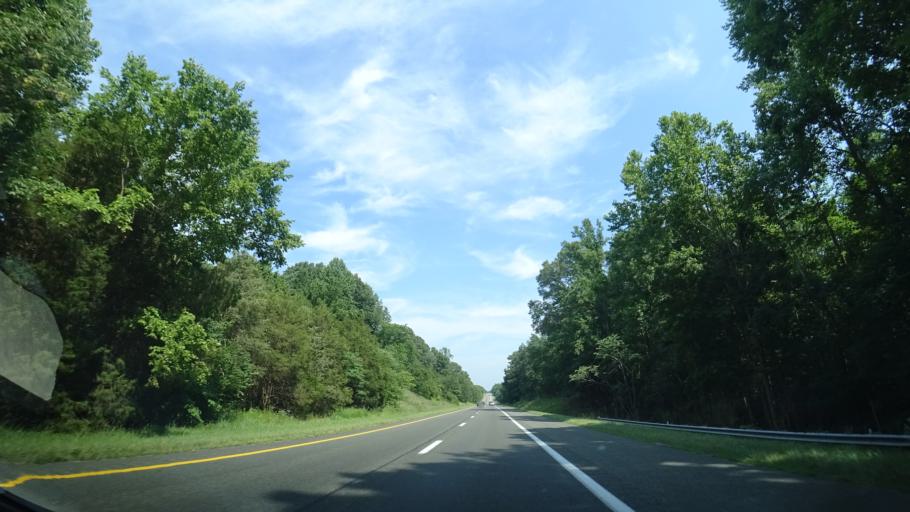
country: US
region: Virginia
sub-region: Goochland County
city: Goochland
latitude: 37.8244
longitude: -77.9580
